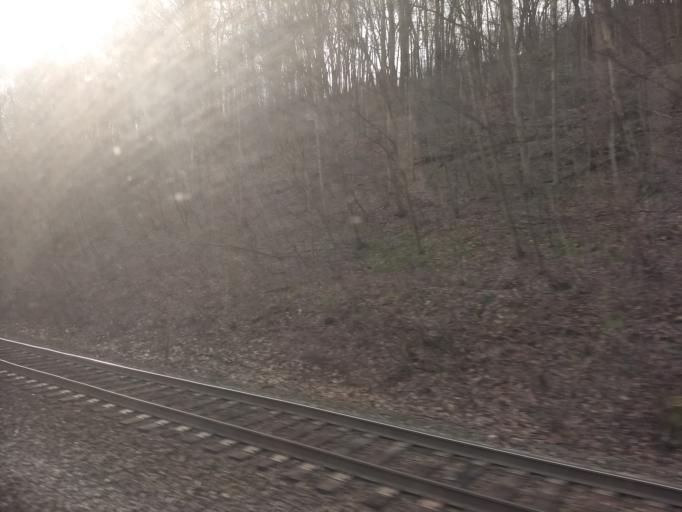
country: US
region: Pennsylvania
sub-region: Cambria County
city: Vinco
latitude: 40.3777
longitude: -78.8476
